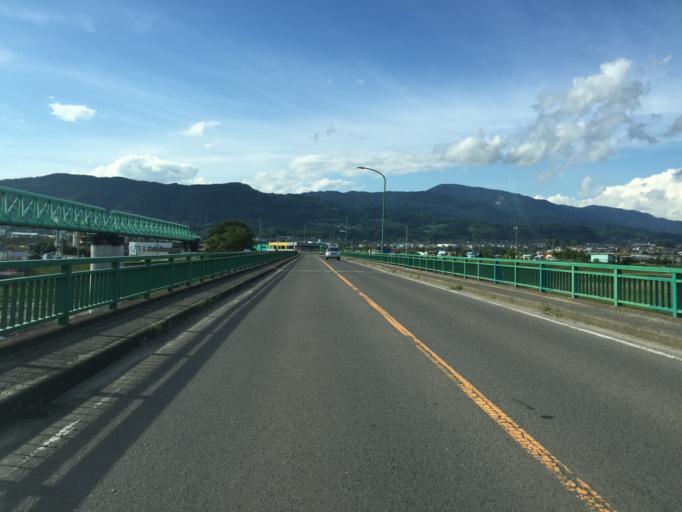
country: JP
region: Fukushima
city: Hobaramachi
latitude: 37.8291
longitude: 140.5194
